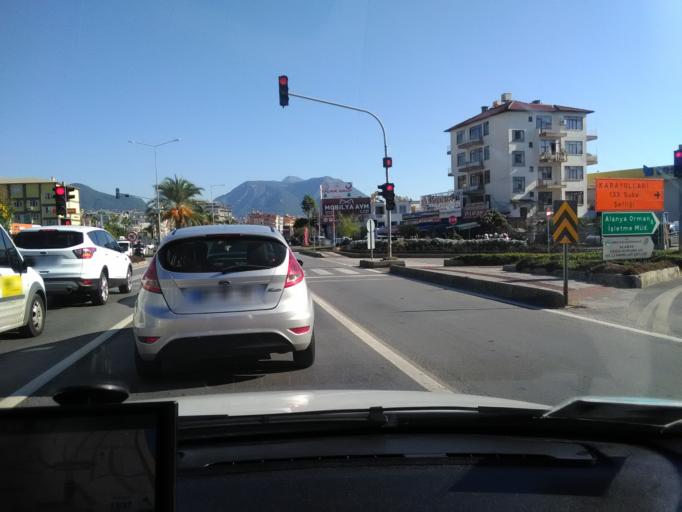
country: TR
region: Antalya
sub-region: Alanya
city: Alanya
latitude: 36.5452
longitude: 32.0230
